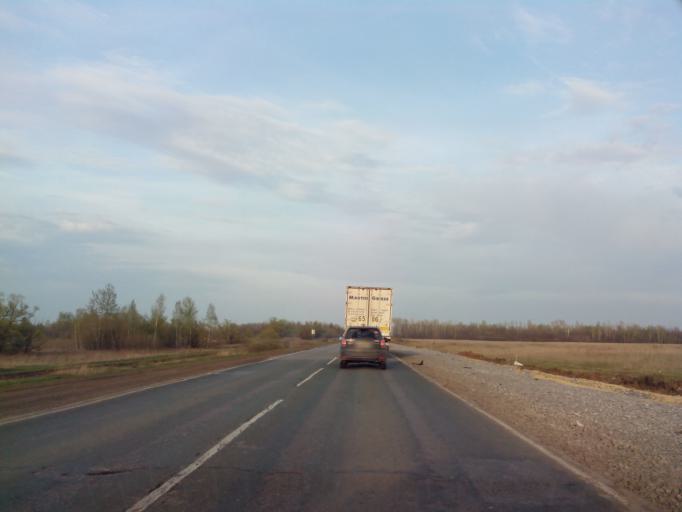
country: RU
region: Rjazan
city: Zarechnyy
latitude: 53.7522
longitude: 39.8223
